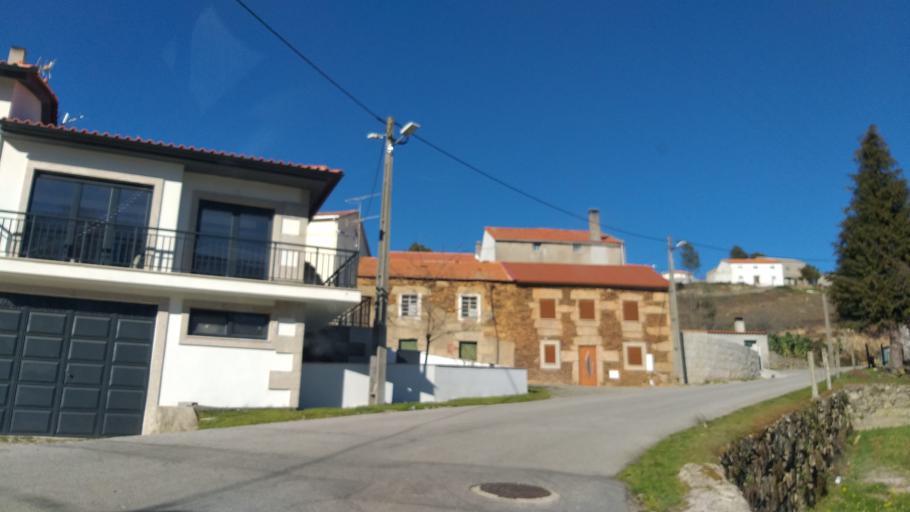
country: PT
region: Guarda
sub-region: Celorico da Beira
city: Celorico da Beira
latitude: 40.5186
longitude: -7.3948
